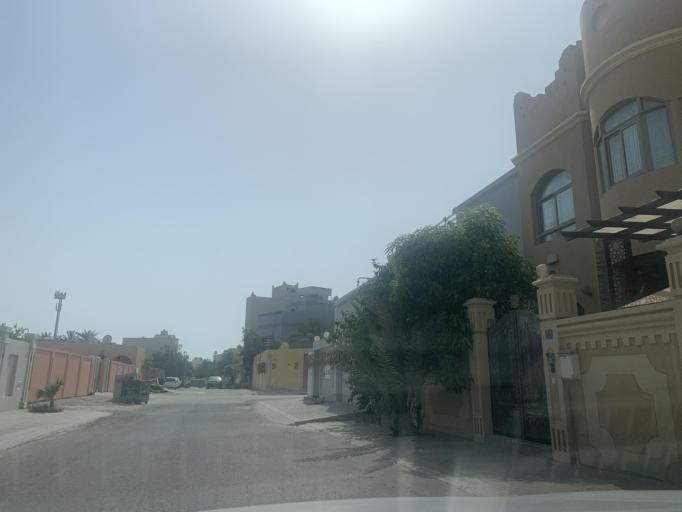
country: BH
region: Manama
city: Jidd Hafs
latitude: 26.2212
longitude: 50.4713
